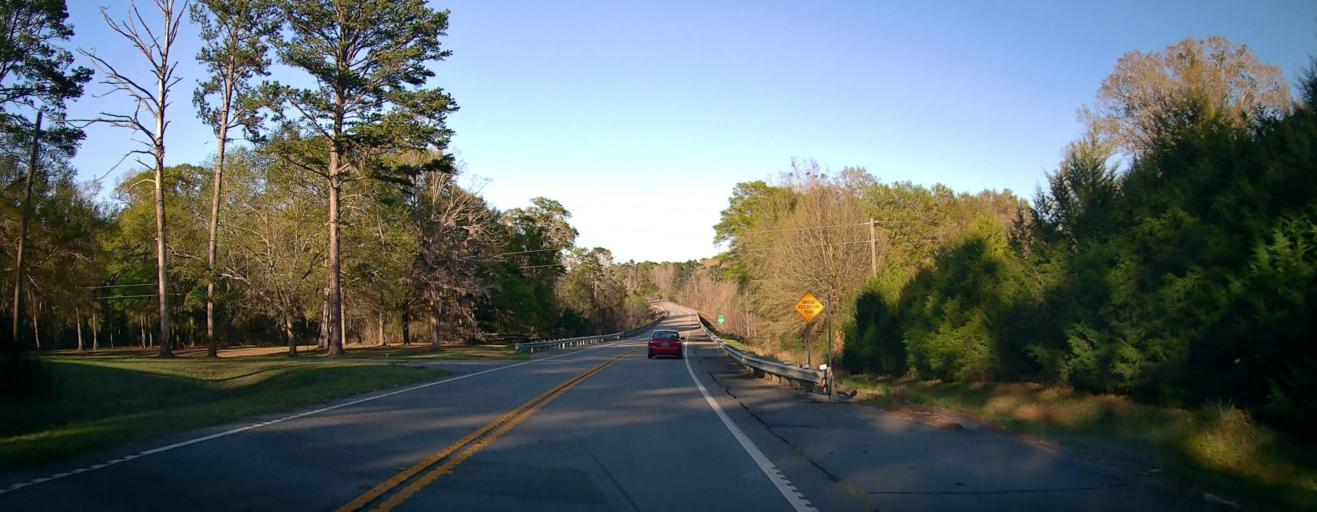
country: US
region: Georgia
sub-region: Pulaski County
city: Hawkinsville
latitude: 32.2607
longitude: -83.5633
